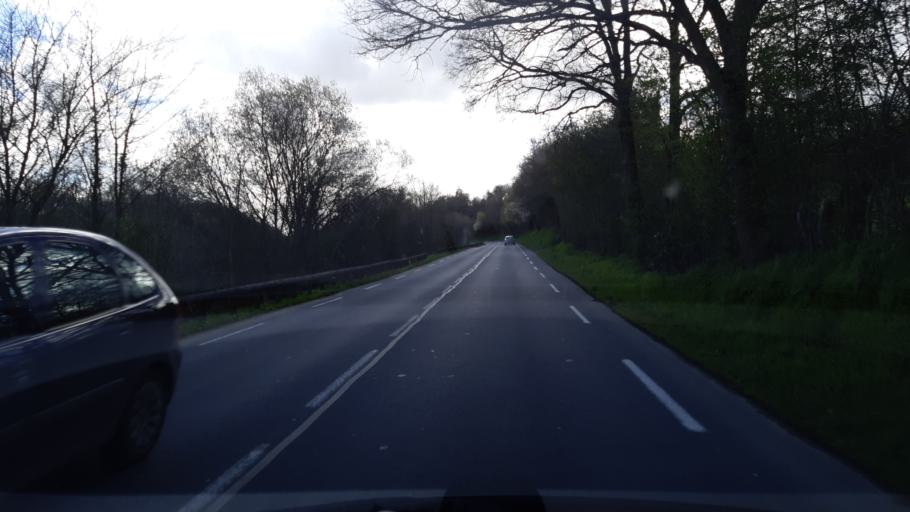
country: FR
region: Lower Normandy
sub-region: Departement de la Manche
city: Agneaux
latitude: 49.0788
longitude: -1.1220
